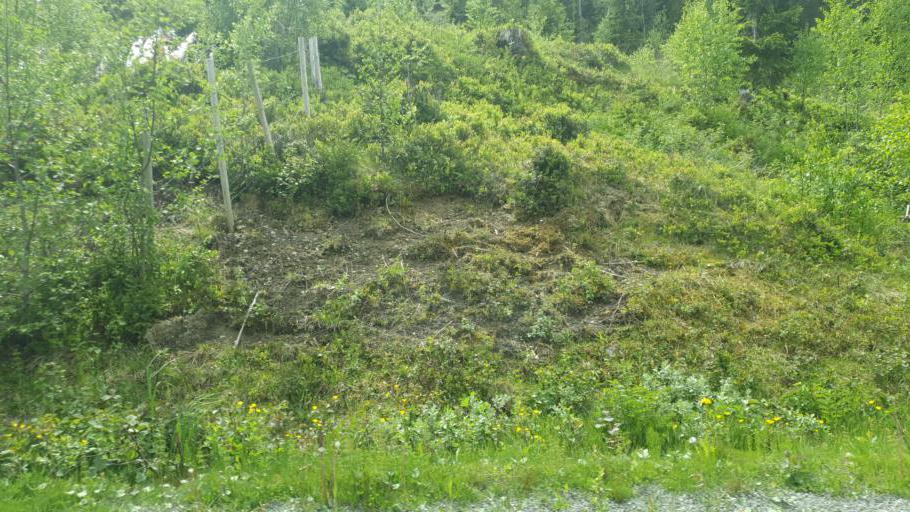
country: NO
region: Nord-Trondelag
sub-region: Leksvik
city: Leksvik
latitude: 63.6909
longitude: 10.5174
